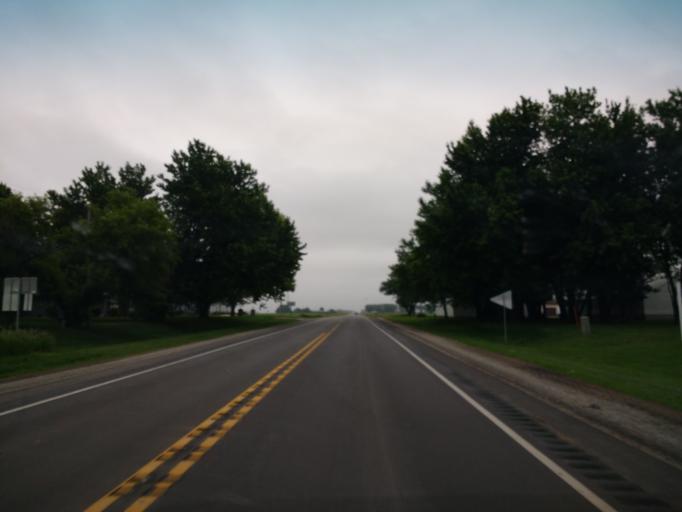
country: US
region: Iowa
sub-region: O'Brien County
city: Sanborn
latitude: 43.1861
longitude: -95.6392
